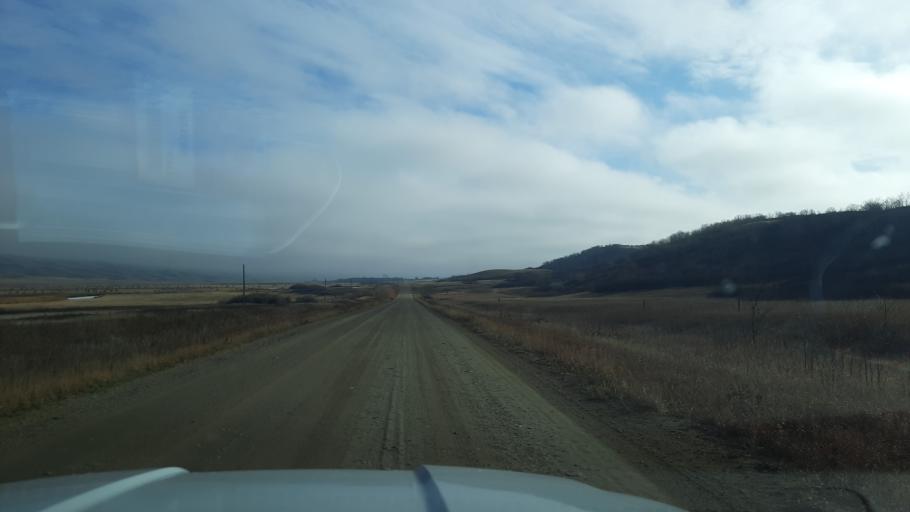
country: CA
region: Saskatchewan
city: Pilot Butte
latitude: 50.7844
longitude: -104.2073
